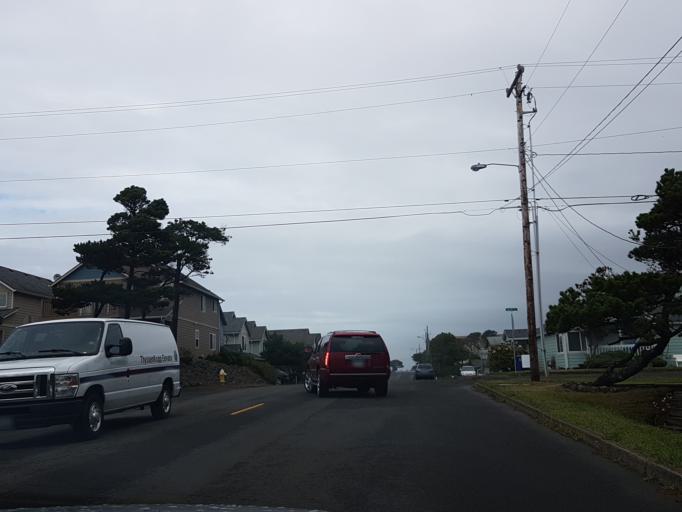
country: US
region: Oregon
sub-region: Lincoln County
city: Newport
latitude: 44.6426
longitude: -124.0594
